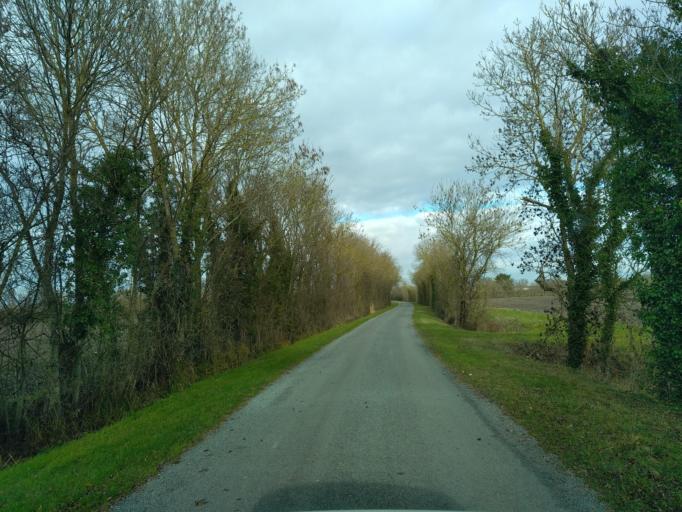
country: FR
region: Pays de la Loire
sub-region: Departement de la Vendee
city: Maillezais
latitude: 46.3375
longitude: -0.7886
